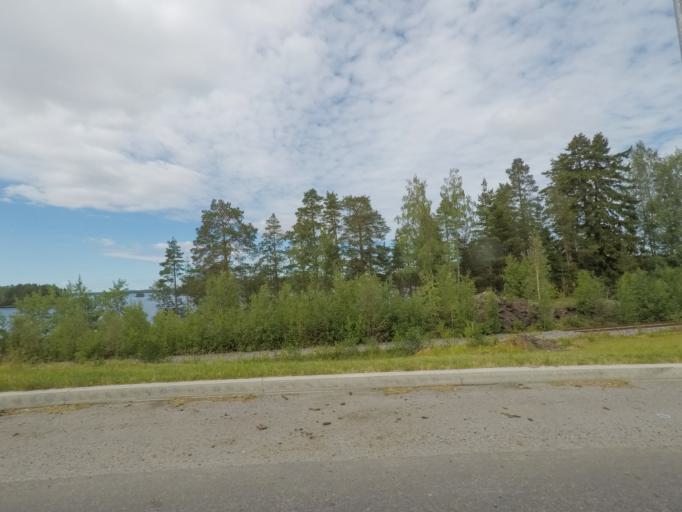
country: FI
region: Southern Savonia
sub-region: Savonlinna
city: Savonlinna
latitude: 61.8803
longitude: 28.8493
